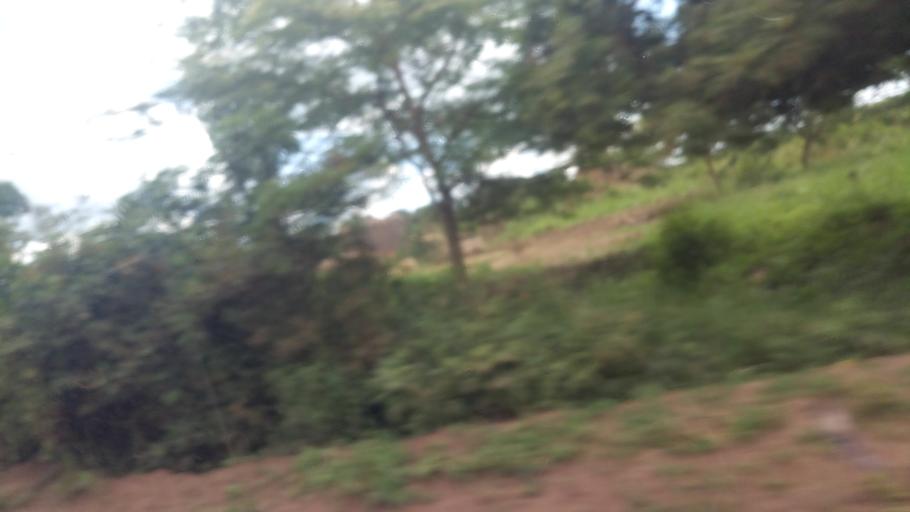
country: UG
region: Western Region
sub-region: Kiryandongo District
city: Kiryandongo
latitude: 1.9289
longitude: 32.1325
